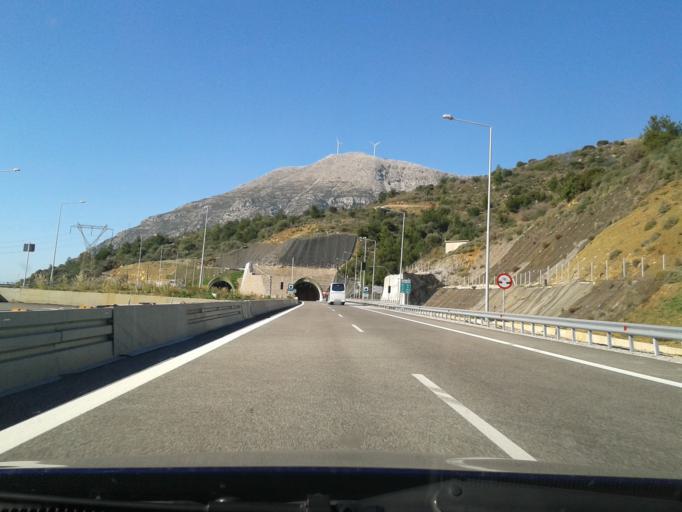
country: GR
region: West Greece
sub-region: Nomos Aitolias kai Akarnanias
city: Antirrio
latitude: 38.3526
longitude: 21.7288
